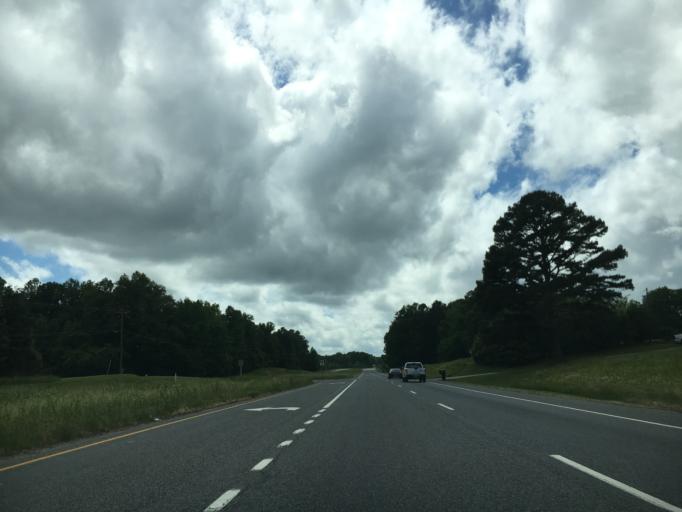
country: US
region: Virginia
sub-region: Mecklenburg County
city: Boydton
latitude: 36.6562
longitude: -78.4481
